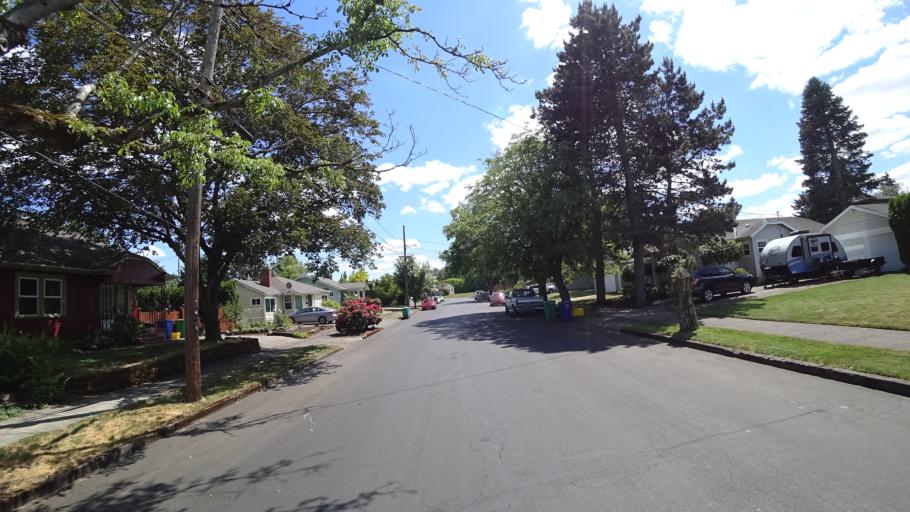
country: US
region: Oregon
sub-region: Washington County
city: West Haven
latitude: 45.5875
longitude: -122.7292
